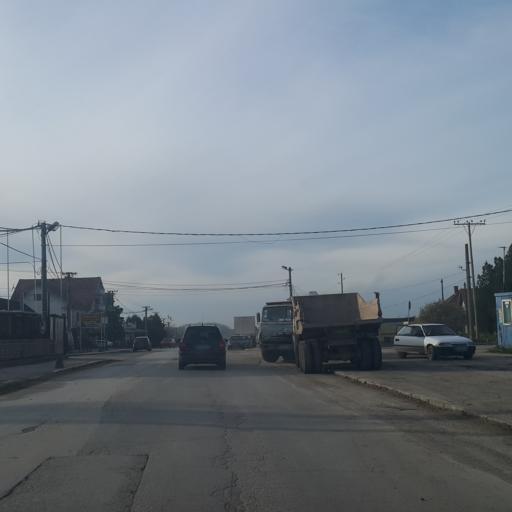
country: RS
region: Central Serbia
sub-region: Belgrade
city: Lazarevac
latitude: 44.3991
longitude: 20.3702
